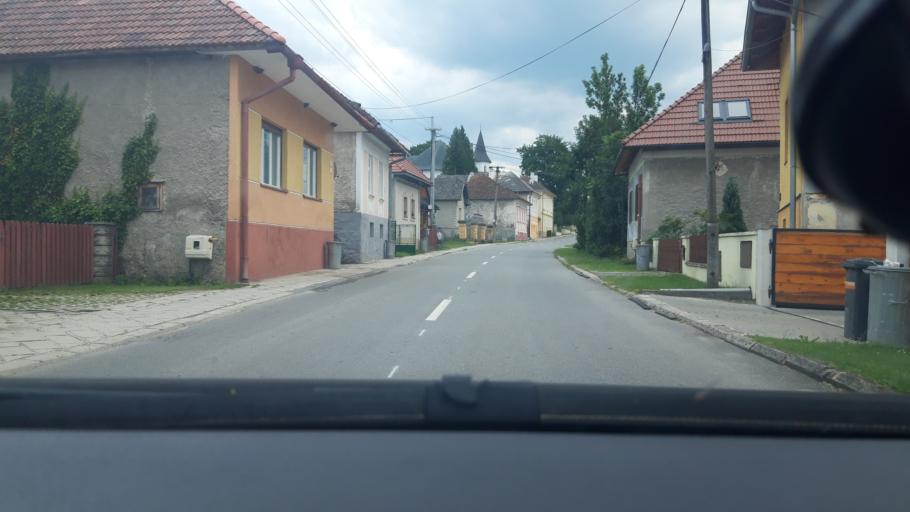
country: SK
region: Zilinsky
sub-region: Okres Martin
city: Martin
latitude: 48.9126
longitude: 18.8854
